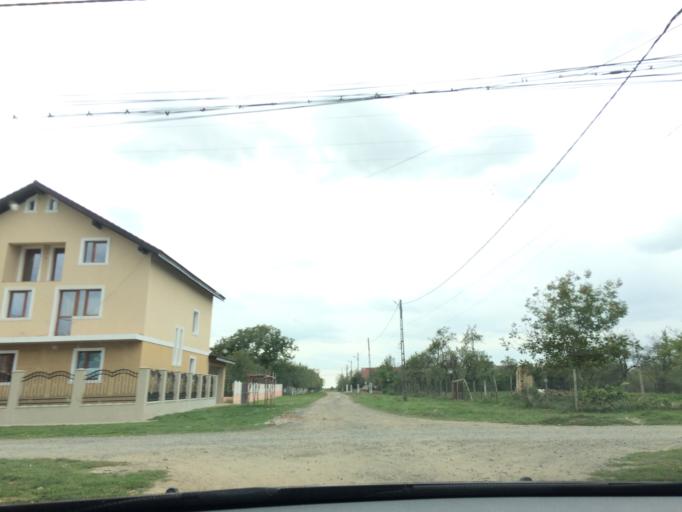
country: RO
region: Timis
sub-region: Oras Recas
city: Recas
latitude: 45.7339
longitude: 21.4926
